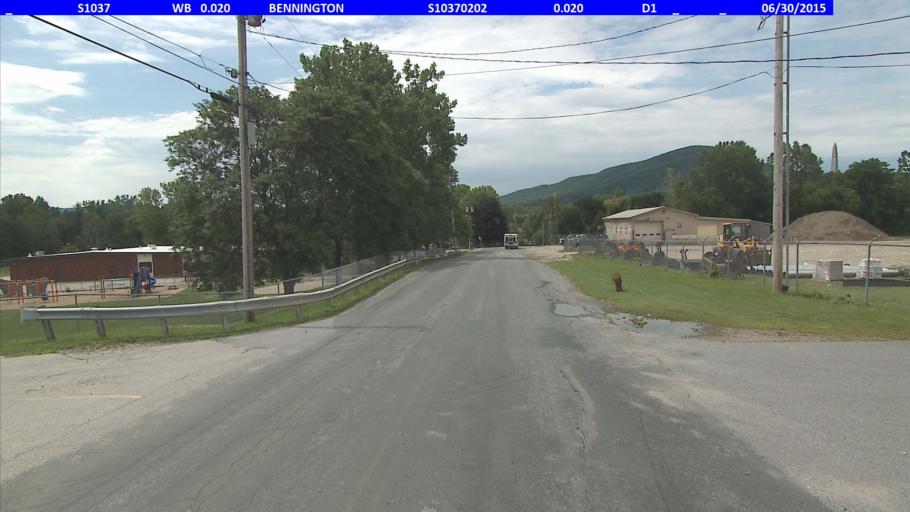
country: US
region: Vermont
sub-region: Bennington County
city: Bennington
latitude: 42.8997
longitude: -73.2026
